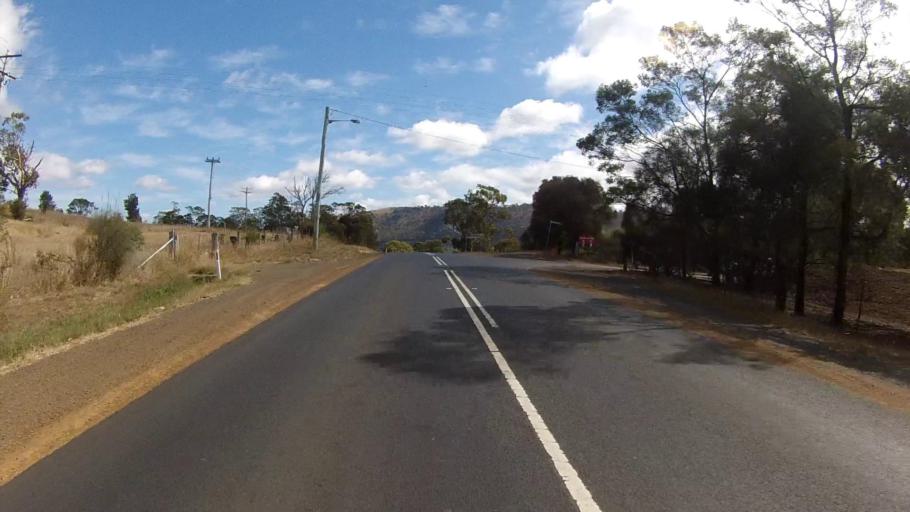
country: AU
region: Tasmania
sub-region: Brighton
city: Old Beach
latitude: -42.7302
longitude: 147.2886
